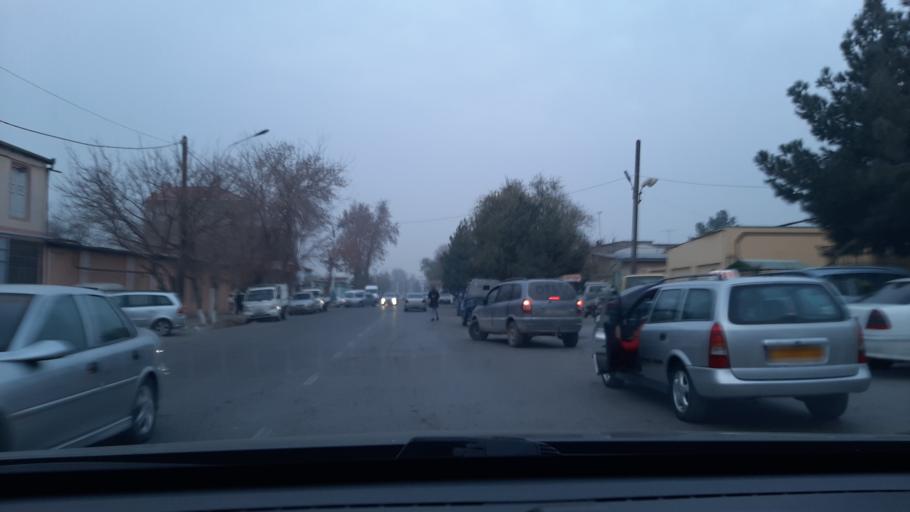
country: TJ
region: Viloyati Sughd
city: Khujand
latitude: 40.2659
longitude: 69.6005
